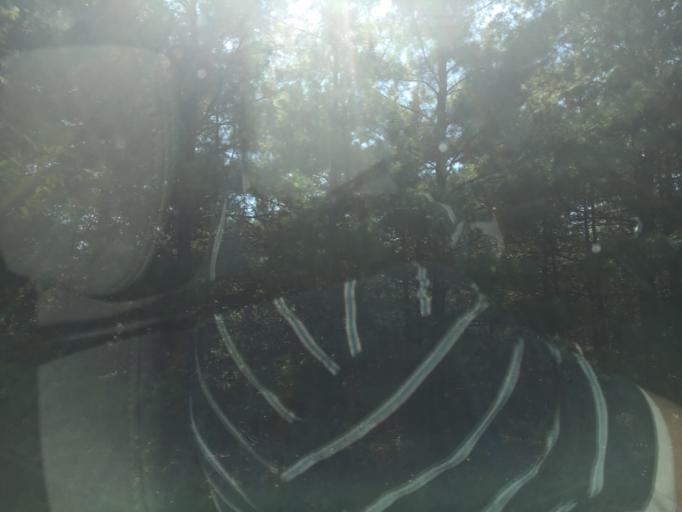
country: US
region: South Carolina
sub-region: Spartanburg County
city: Wellford
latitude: 34.8990
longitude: -82.0829
